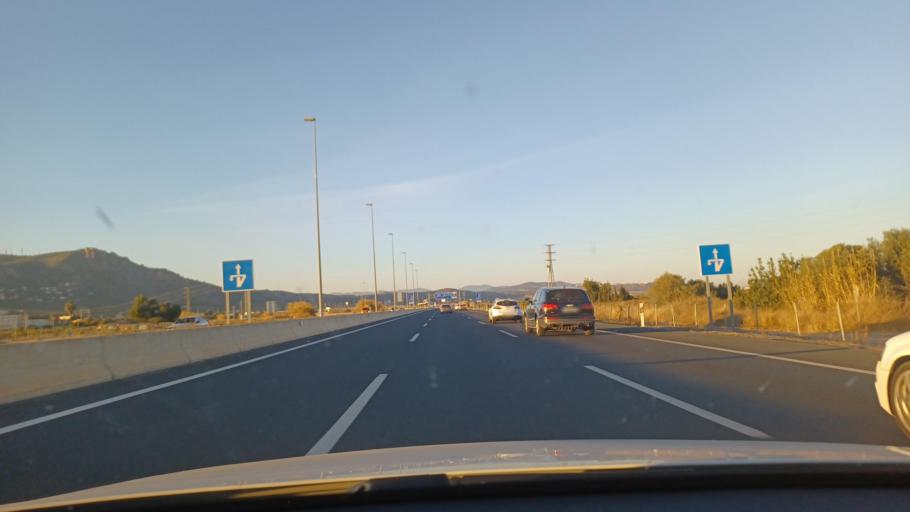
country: ES
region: Valencia
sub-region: Provincia de Valencia
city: Pucol
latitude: 39.6174
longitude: -0.2947
